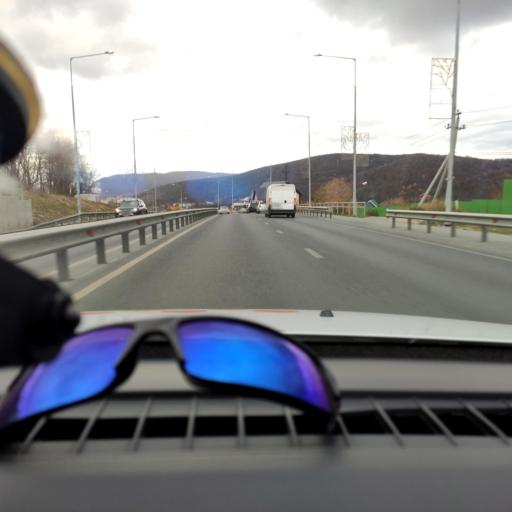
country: RU
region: Samara
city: Volzhskiy
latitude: 53.3675
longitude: 50.1930
